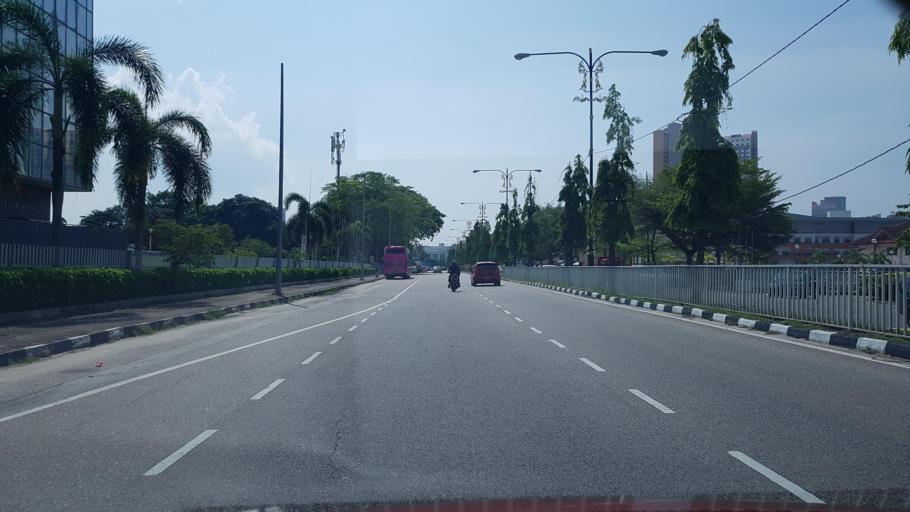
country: MY
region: Terengganu
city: Kuala Terengganu
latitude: 5.3245
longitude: 103.1497
